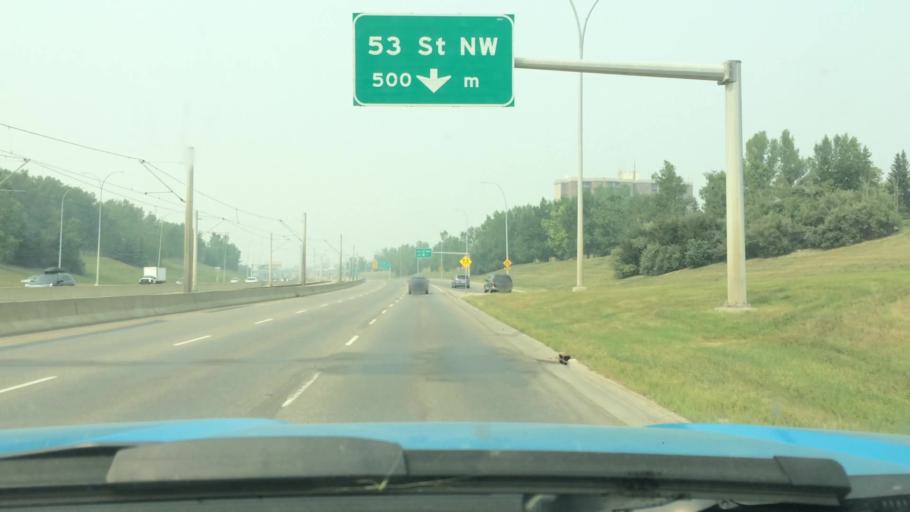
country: CA
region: Alberta
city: Calgary
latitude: 51.0993
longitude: -114.1512
